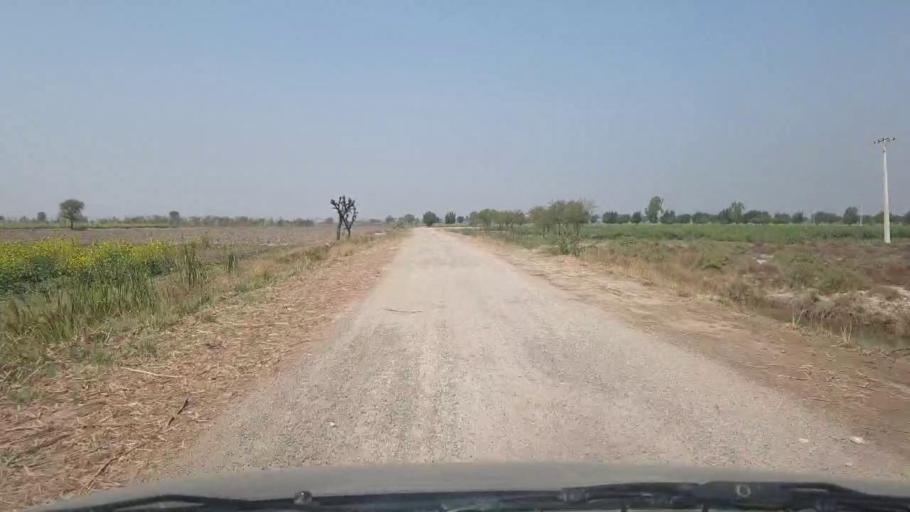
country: PK
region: Sindh
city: Mirwah Gorchani
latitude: 25.3470
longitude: 69.1408
